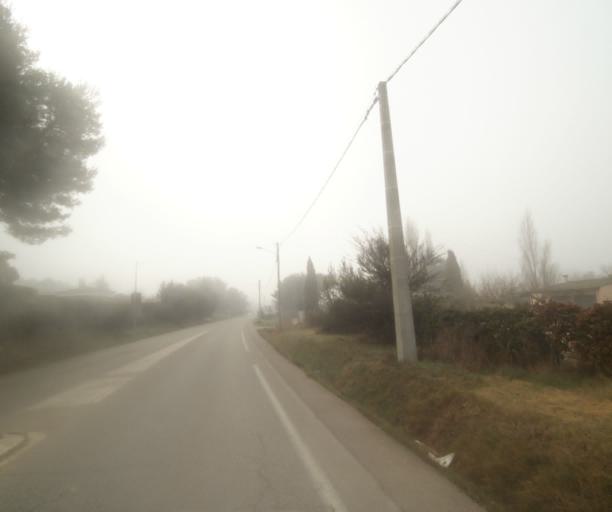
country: FR
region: Provence-Alpes-Cote d'Azur
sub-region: Departement des Bouches-du-Rhone
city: Eguilles
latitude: 43.5449
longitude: 5.3679
